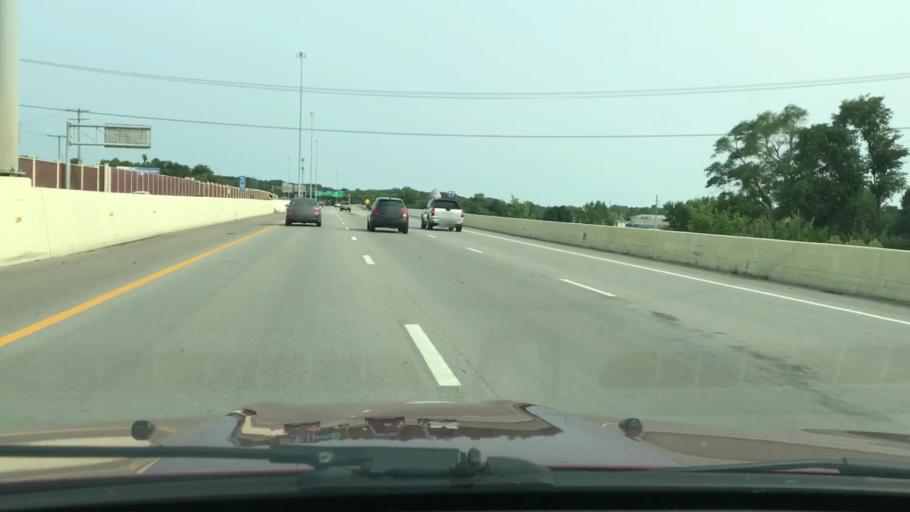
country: US
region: Ohio
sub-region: Stark County
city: Canton
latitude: 40.7926
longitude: -81.3884
